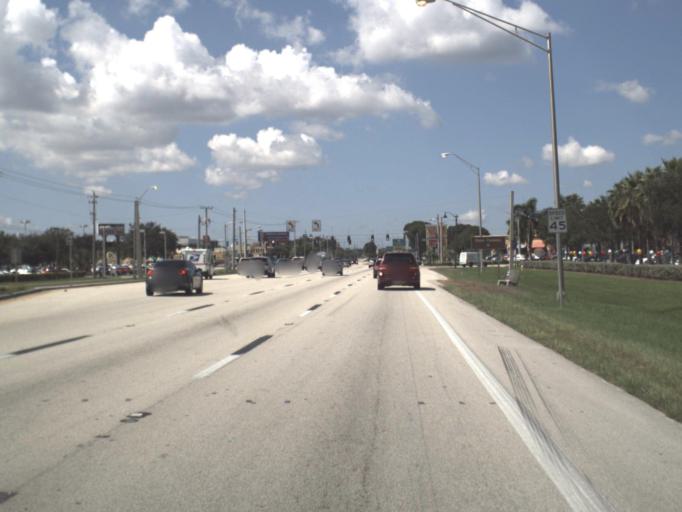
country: US
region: Florida
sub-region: Lee County
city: Pine Manor
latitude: 26.5973
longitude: -81.8604
